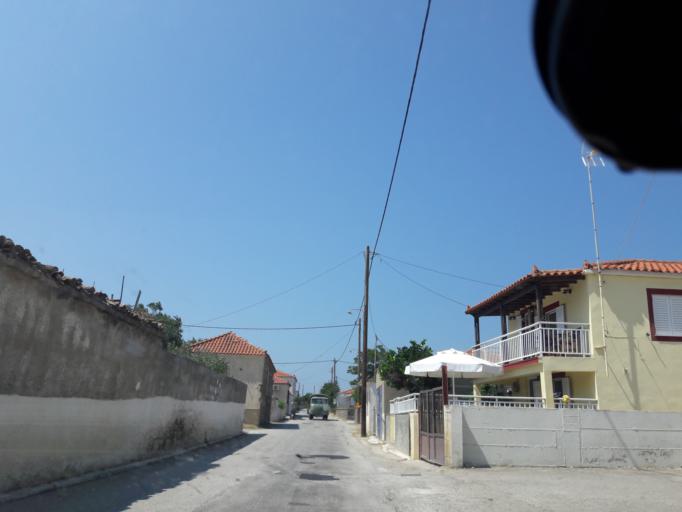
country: GR
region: North Aegean
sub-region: Nomos Lesvou
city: Myrina
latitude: 39.9235
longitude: 25.2998
